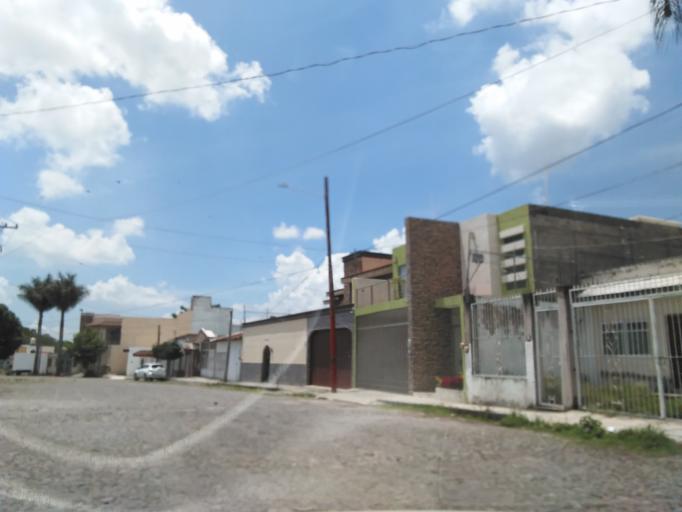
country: MX
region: Nayarit
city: Tepic
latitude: 21.5117
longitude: -104.9144
